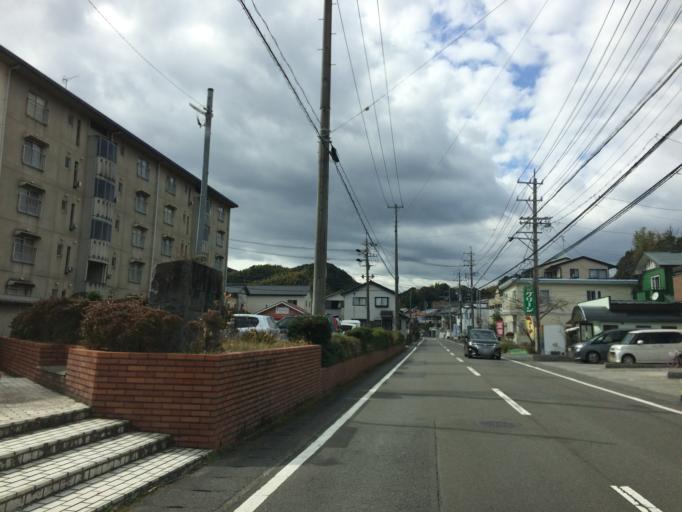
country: JP
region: Shizuoka
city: Fujieda
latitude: 34.8662
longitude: 138.2389
